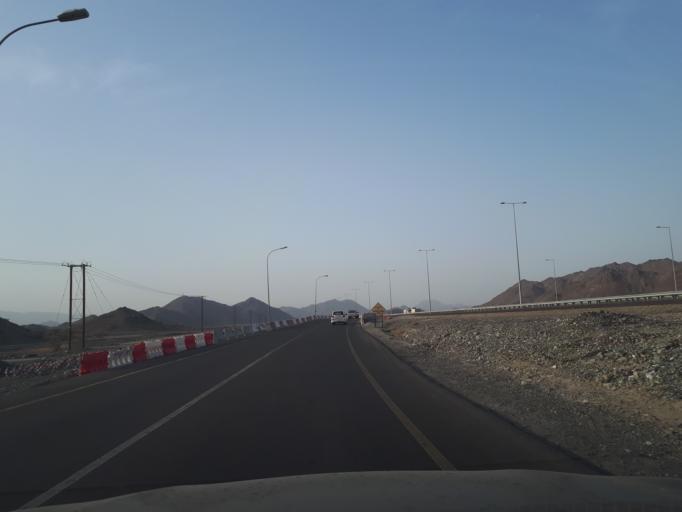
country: OM
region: Muhafazat ad Dakhiliyah
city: Sufalat Sama'il
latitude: 23.2902
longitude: 58.1091
